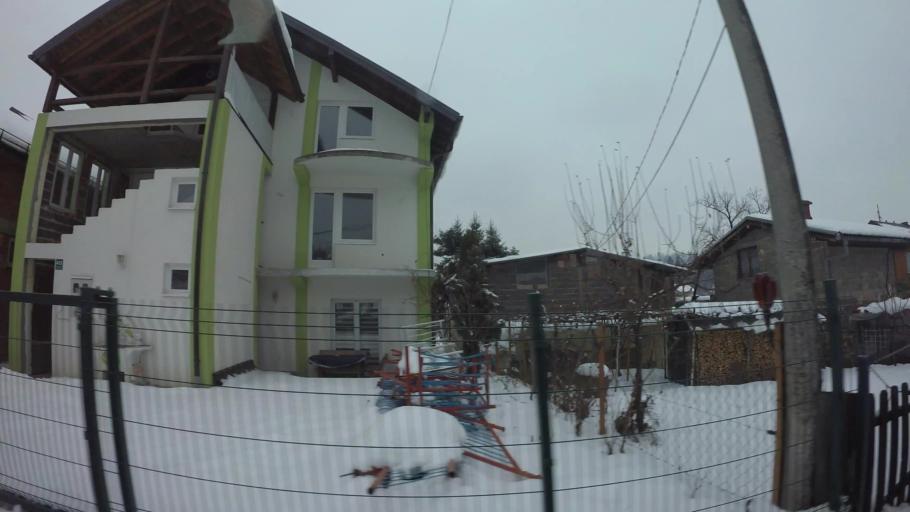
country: BA
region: Federation of Bosnia and Herzegovina
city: Hadzici
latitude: 43.8618
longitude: 18.2699
